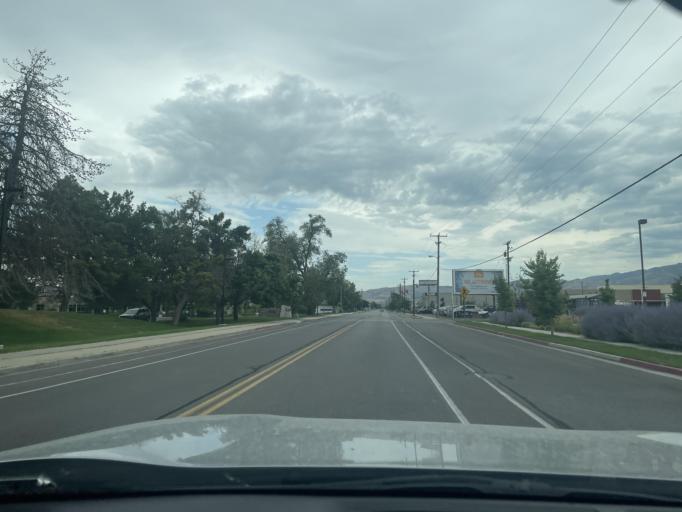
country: US
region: Utah
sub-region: Salt Lake County
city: Centerfield
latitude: 40.6891
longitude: -111.8911
